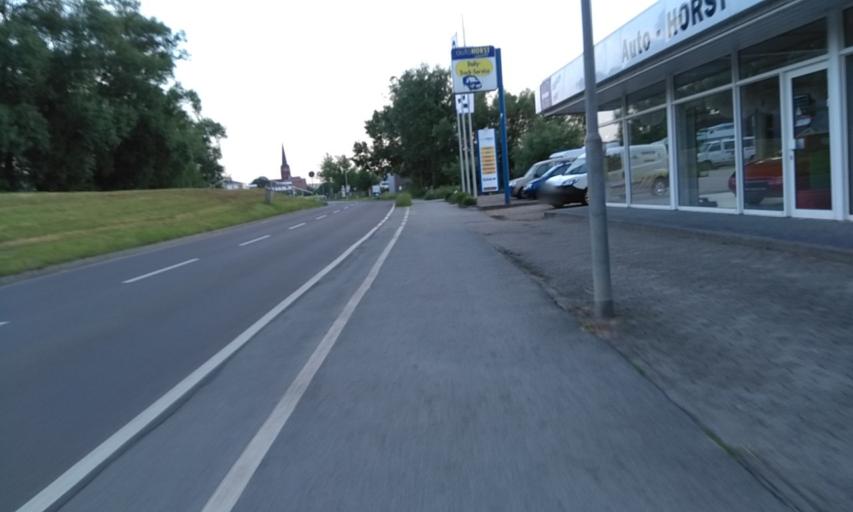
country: DE
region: Lower Saxony
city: Buxtehude
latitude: 53.4844
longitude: 9.7044
